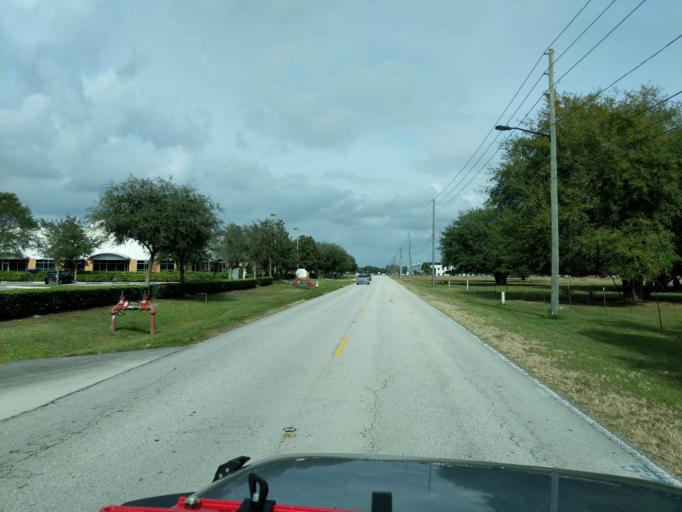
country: US
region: Florida
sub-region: Orange County
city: Ocoee
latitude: 28.5738
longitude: -81.5609
